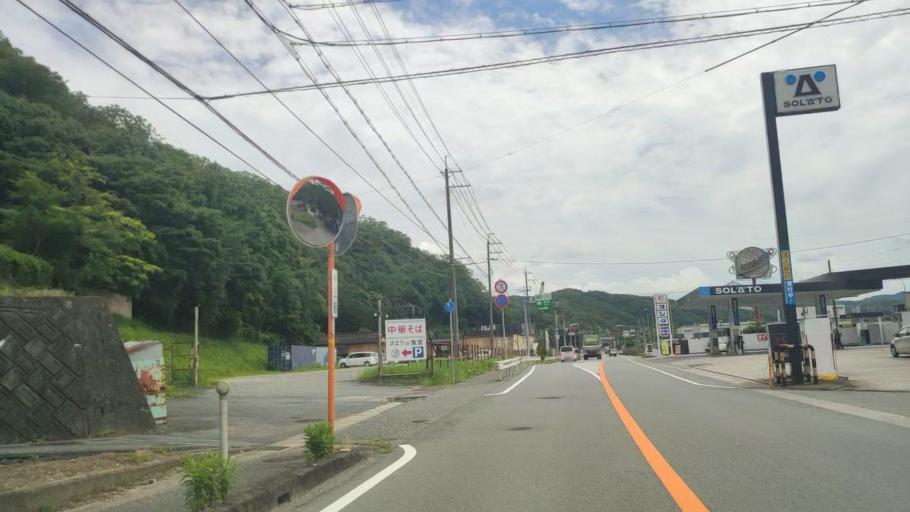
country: JP
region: Hyogo
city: Yamazakicho-nakabirose
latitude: 35.0254
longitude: 134.3711
